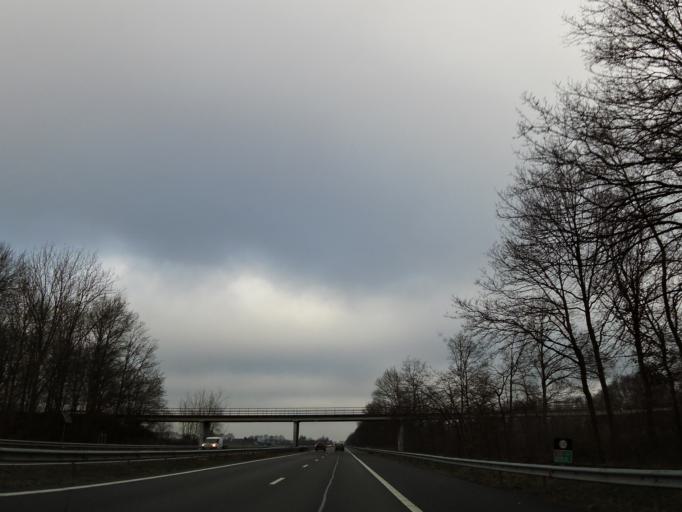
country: NL
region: Limburg
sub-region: Gemeente Leudal
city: Kelpen-Oler
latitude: 51.2043
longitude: 5.8255
